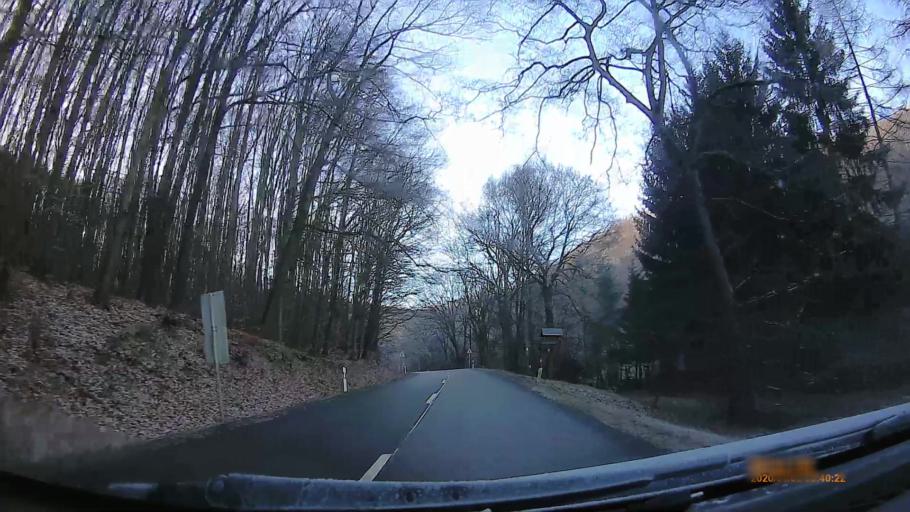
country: HU
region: Heves
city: Paradsasvar
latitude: 47.9173
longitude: 19.9941
